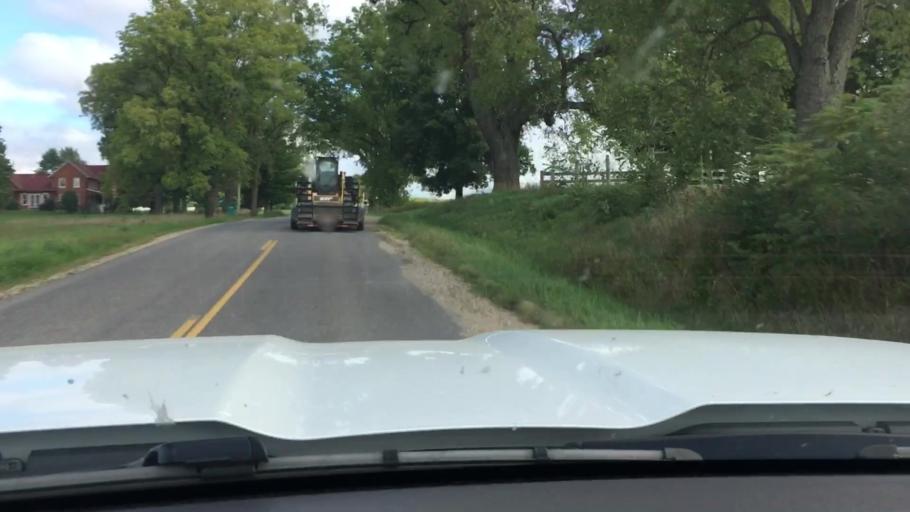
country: US
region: Michigan
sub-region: Kent County
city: Byron Center
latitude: 42.8087
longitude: -85.8027
